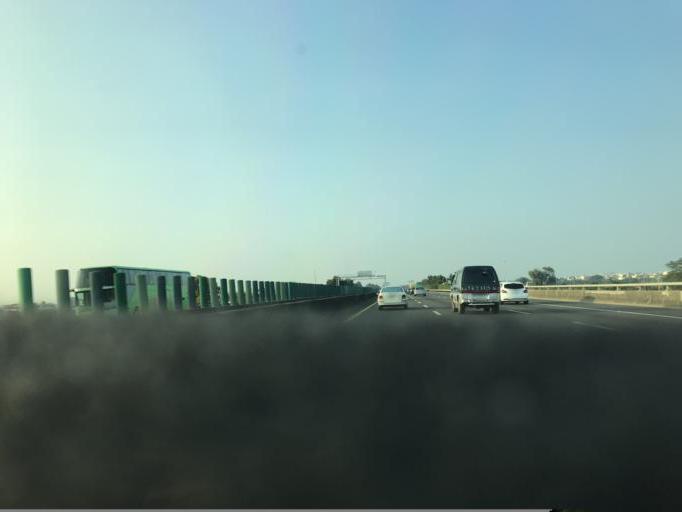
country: TW
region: Taiwan
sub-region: Tainan
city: Tainan
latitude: 23.1328
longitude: 120.2368
